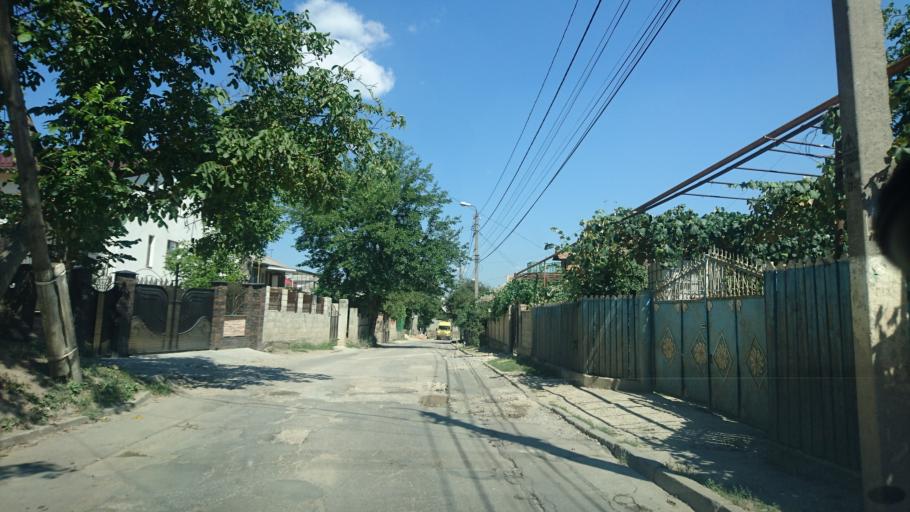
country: MD
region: Chisinau
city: Vatra
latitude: 47.0148
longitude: 28.7668
